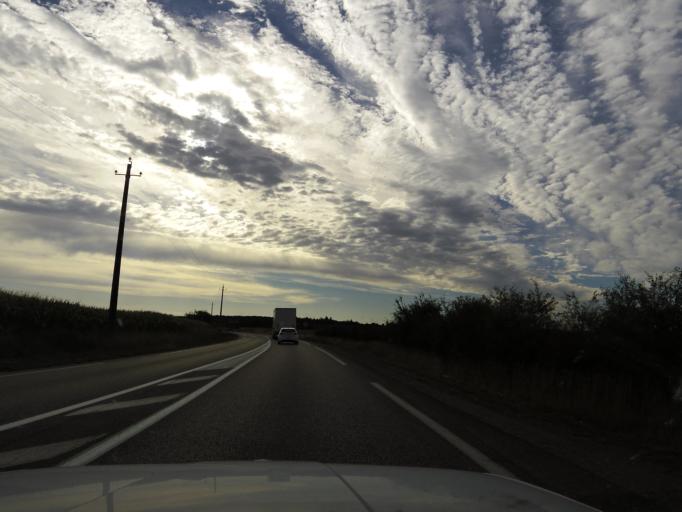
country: FR
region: Rhone-Alpes
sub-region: Departement de l'Ain
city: Chazey-sur-Ain
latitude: 45.8577
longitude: 5.2468
